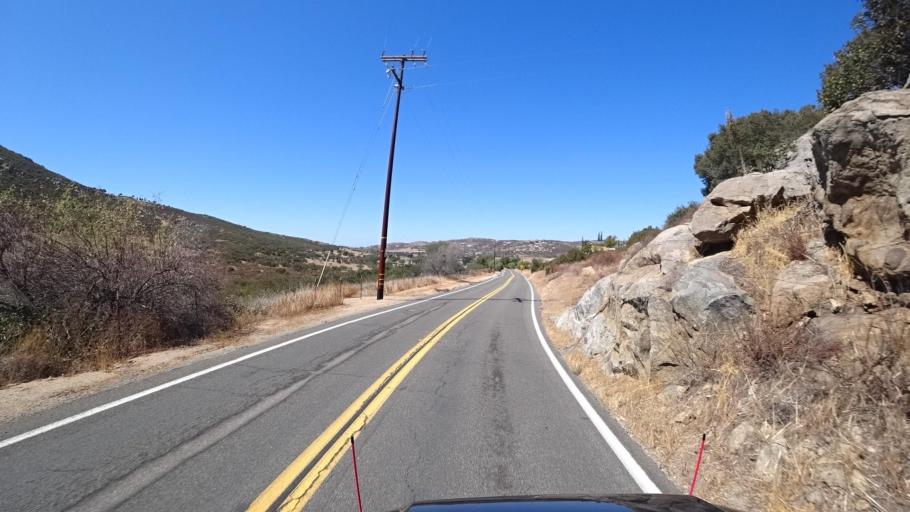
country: US
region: California
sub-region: San Diego County
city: San Diego Country Estates
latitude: 33.0489
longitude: -116.7918
